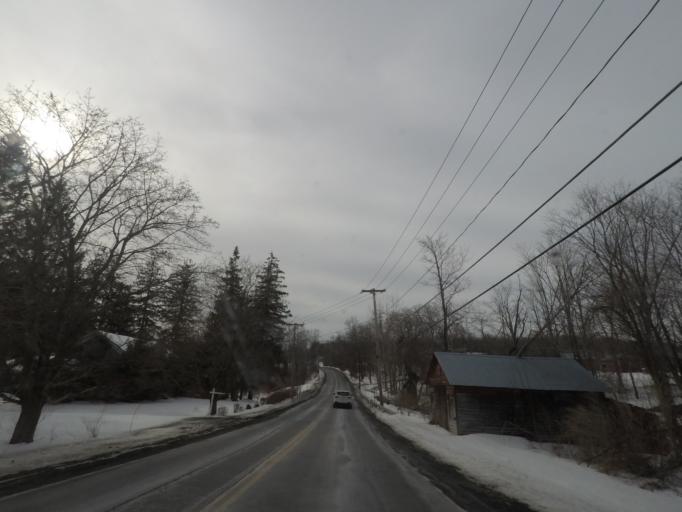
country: US
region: New York
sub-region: Albany County
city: Altamont
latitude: 42.6658
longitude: -74.1284
